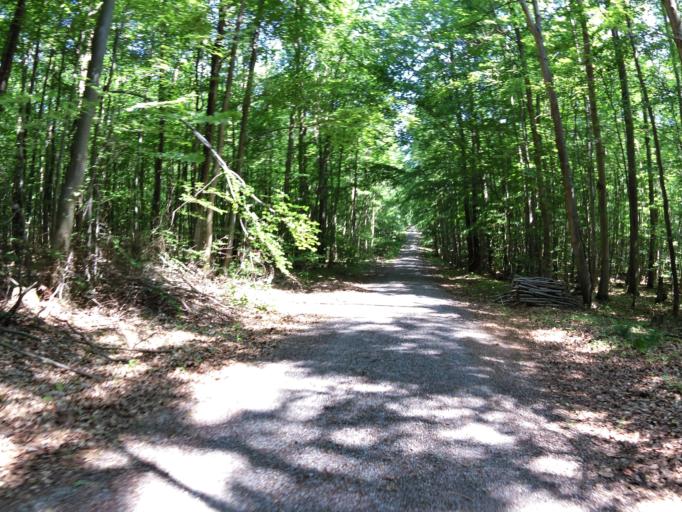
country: DE
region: Bavaria
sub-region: Regierungsbezirk Unterfranken
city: Kist
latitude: 49.7241
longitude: 9.8639
